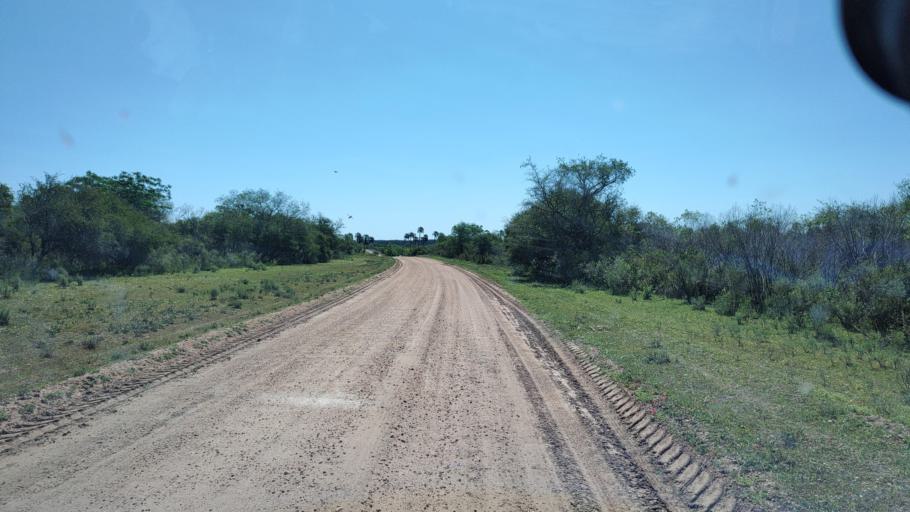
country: AR
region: Entre Rios
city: Ubajay
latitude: -31.8705
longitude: -58.2413
